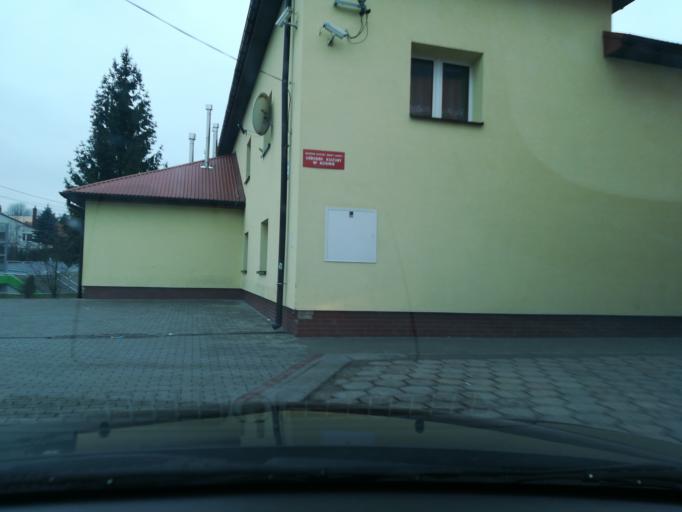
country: PL
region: Subcarpathian Voivodeship
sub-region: Powiat lancucki
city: Kosina
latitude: 50.0717
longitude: 22.3293
